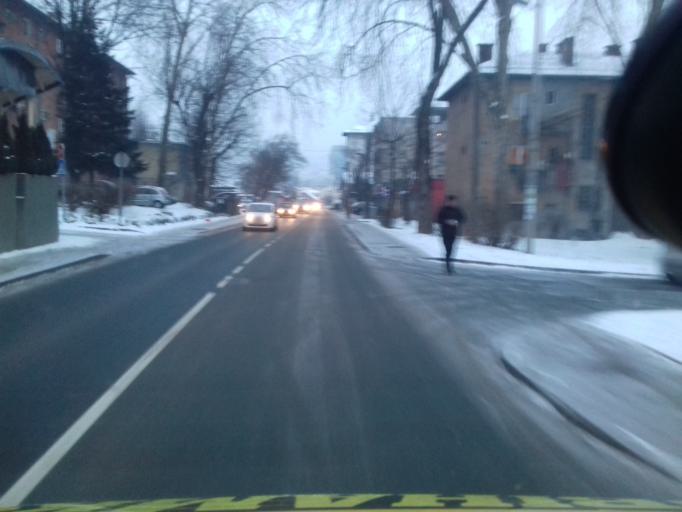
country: BA
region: Federation of Bosnia and Herzegovina
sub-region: Kanton Sarajevo
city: Sarajevo
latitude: 43.8560
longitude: 18.3661
